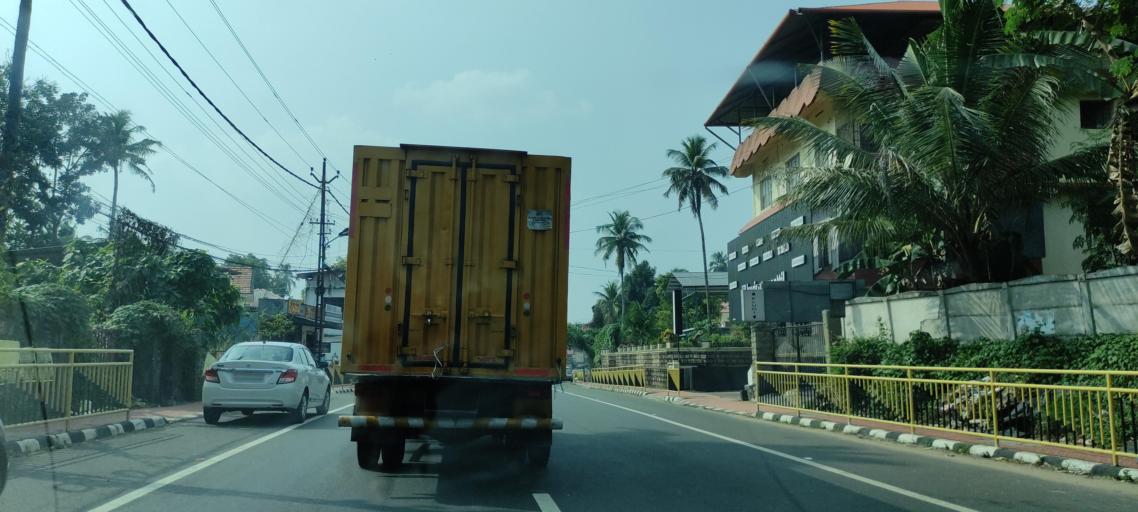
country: IN
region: Kerala
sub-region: Alappuzha
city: Chengannur
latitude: 9.3137
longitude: 76.6198
